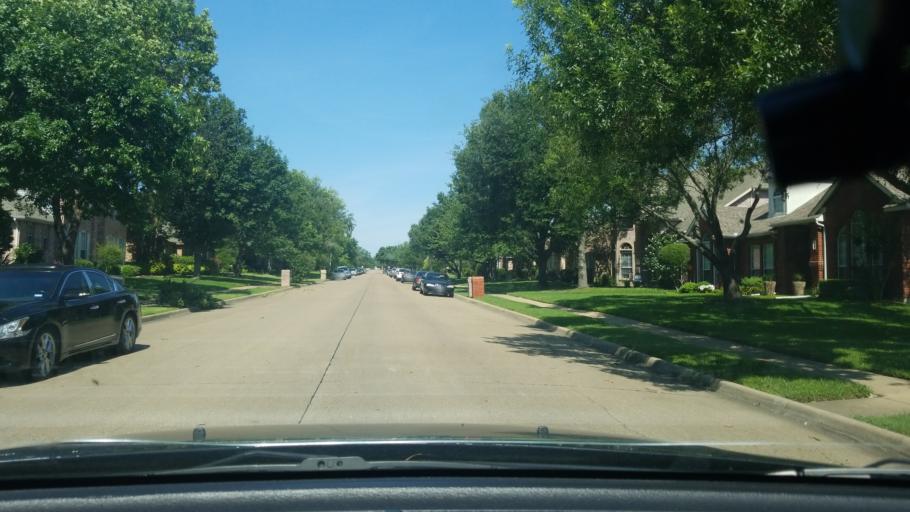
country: US
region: Texas
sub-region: Dallas County
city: Mesquite
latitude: 32.7750
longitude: -96.5860
